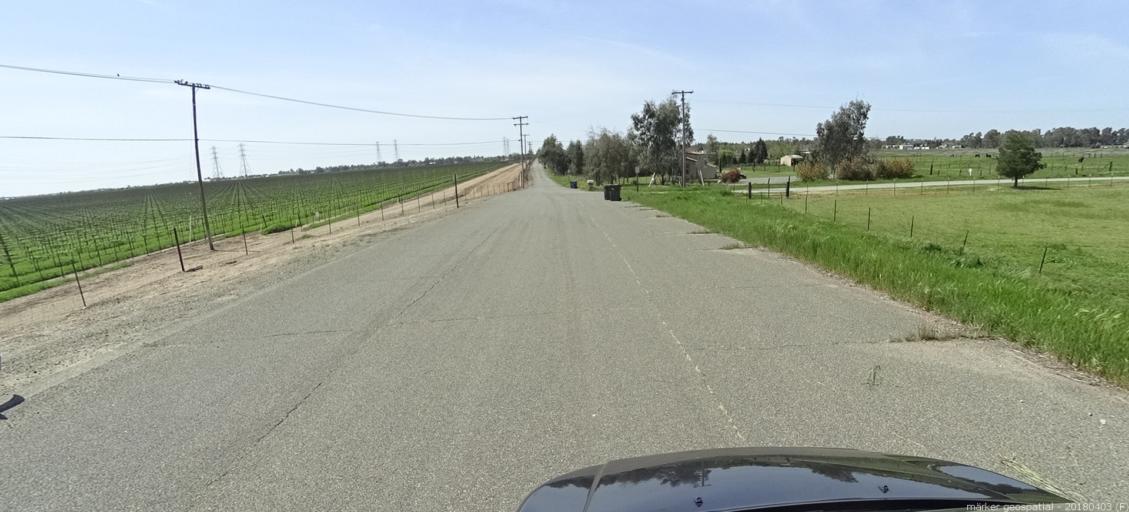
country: US
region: California
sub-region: Sacramento County
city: Clay
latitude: 38.3504
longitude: -121.1909
